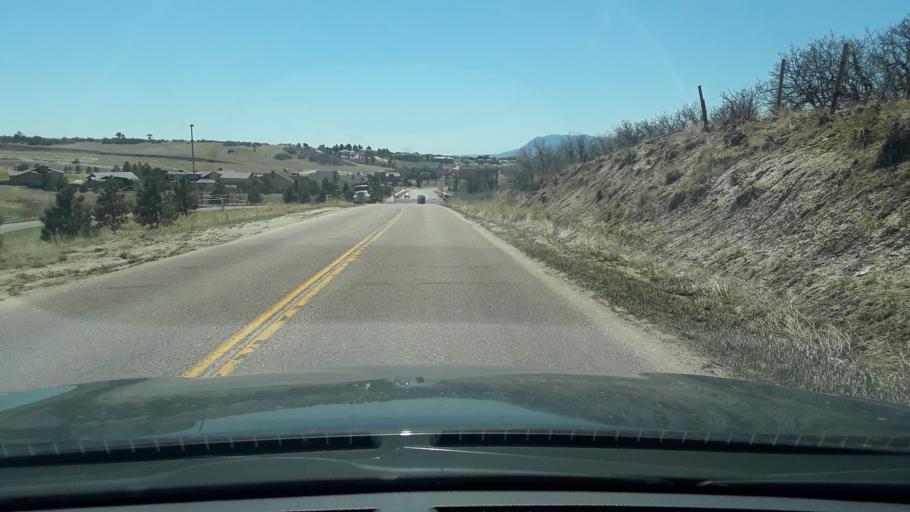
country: US
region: Colorado
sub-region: El Paso County
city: Gleneagle
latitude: 39.0299
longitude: -104.7991
